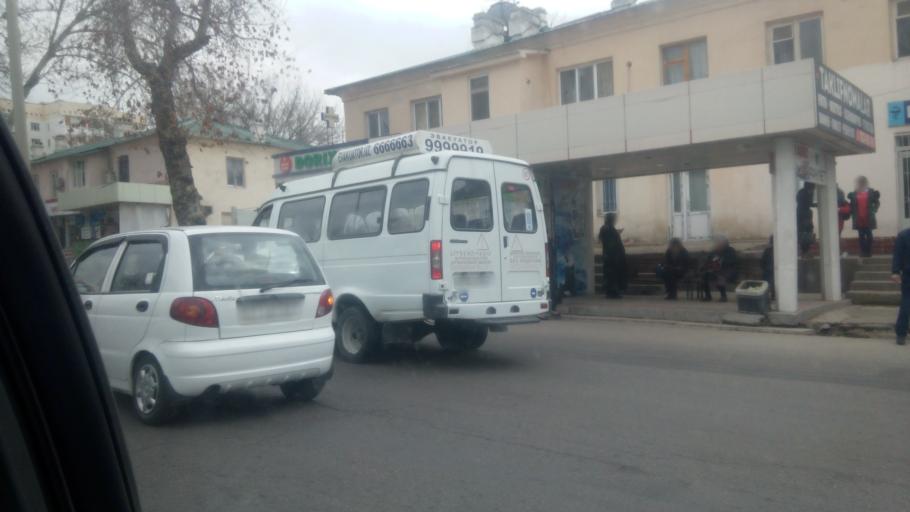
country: UZ
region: Toshkent Shahri
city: Tashkent
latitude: 41.3484
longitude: 69.2399
